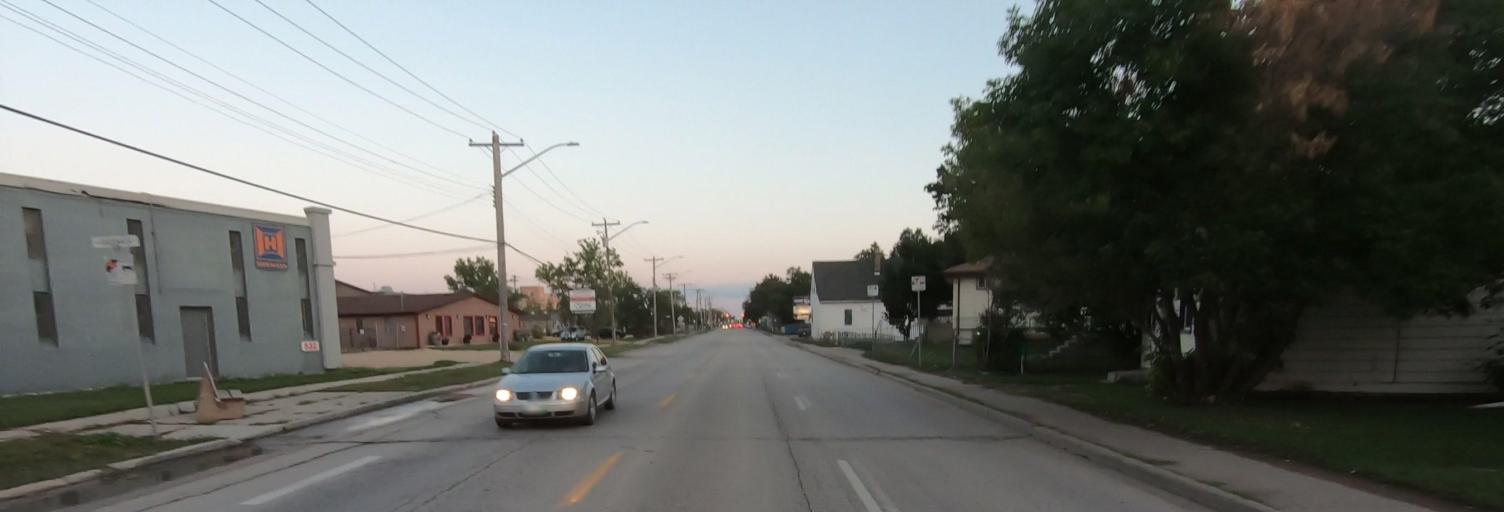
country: CA
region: Manitoba
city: Winnipeg
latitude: 49.8854
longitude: -97.1007
